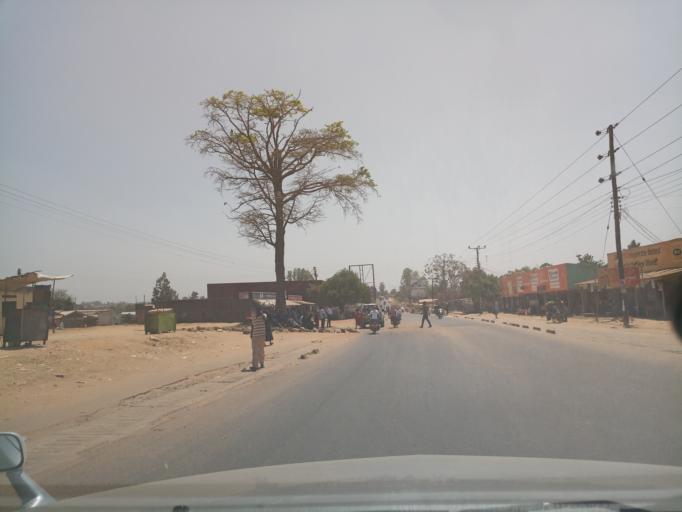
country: UG
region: Northern Region
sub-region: Arua District
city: Arua
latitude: 3.0062
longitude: 30.9113
